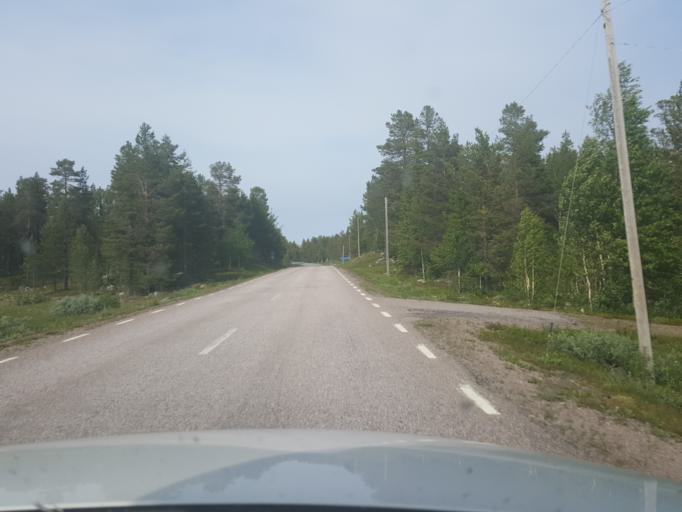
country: SE
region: Norrbotten
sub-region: Arjeplogs Kommun
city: Arjeplog
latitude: 65.8325
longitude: 18.0189
